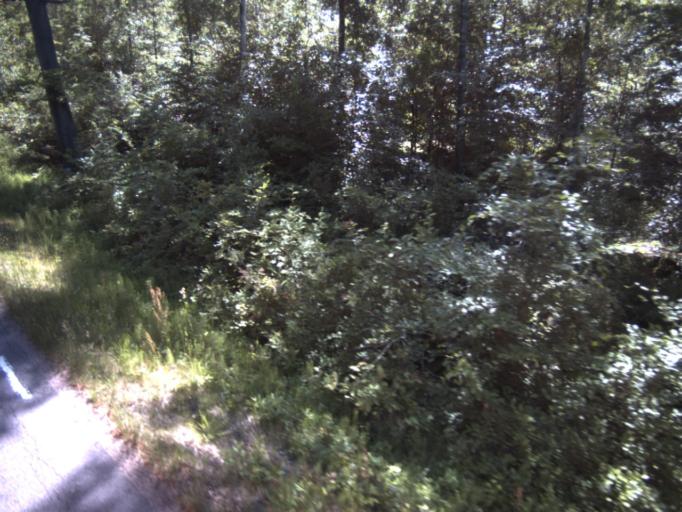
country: SE
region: Skane
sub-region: Helsingborg
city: Helsingborg
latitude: 56.1080
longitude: 12.6587
